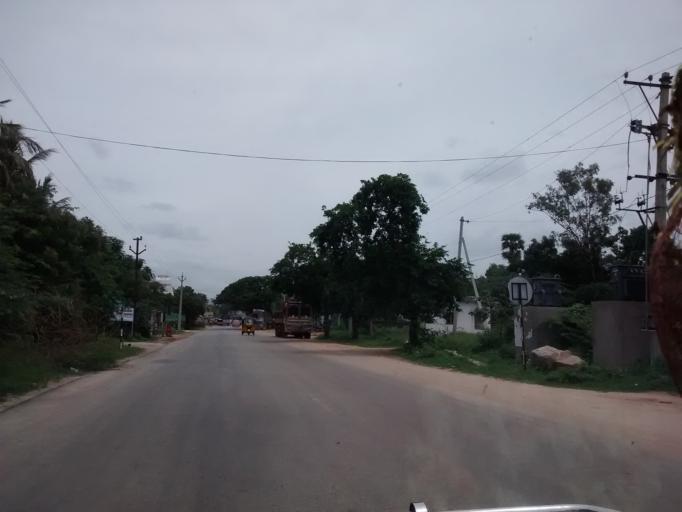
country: IN
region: Andhra Pradesh
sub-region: Chittoor
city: Narasingapuram
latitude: 13.6109
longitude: 79.3309
